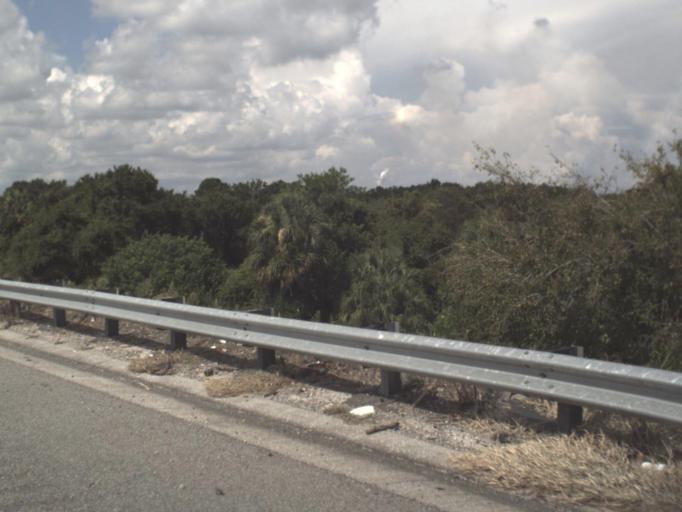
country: US
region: Florida
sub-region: Hillsborough County
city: Gibsonton
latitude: 27.8342
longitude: -82.3500
